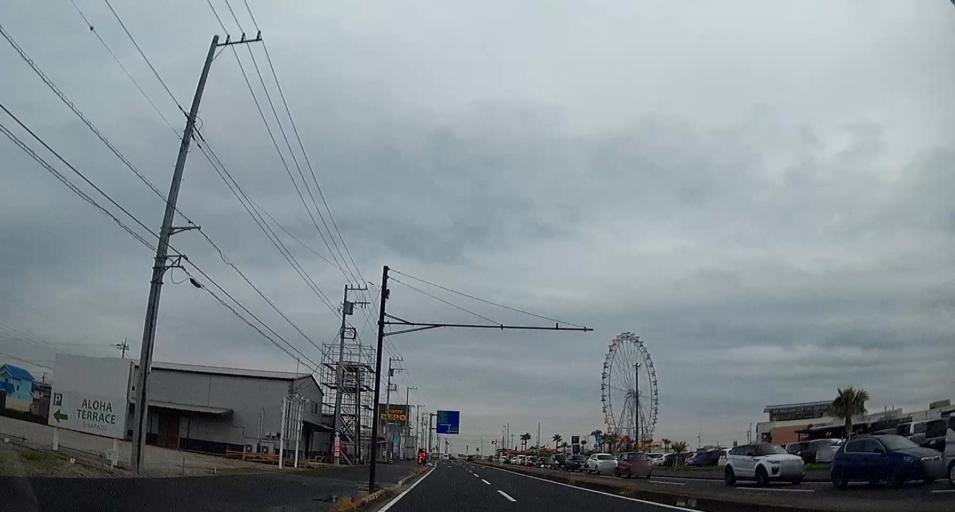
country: JP
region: Chiba
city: Kisarazu
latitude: 35.4366
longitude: 139.9322
